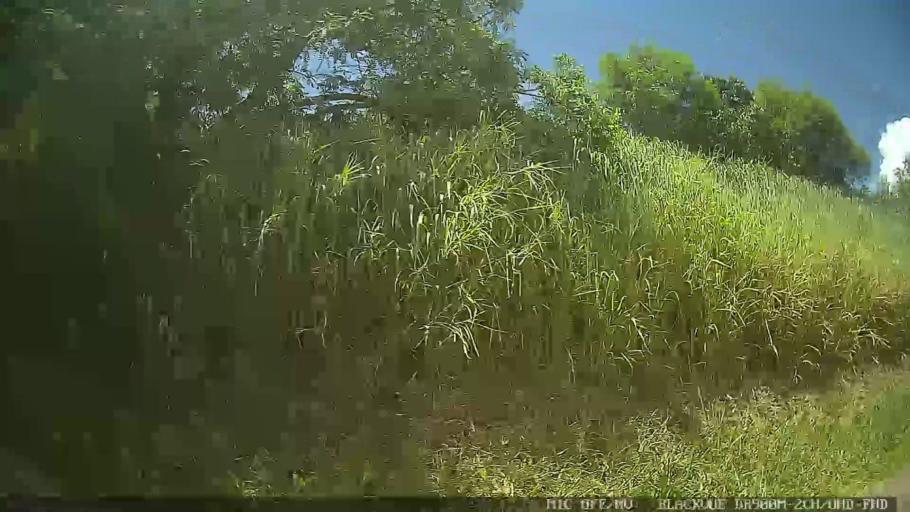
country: BR
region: Sao Paulo
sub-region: Conchas
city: Conchas
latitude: -23.0251
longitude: -48.0162
